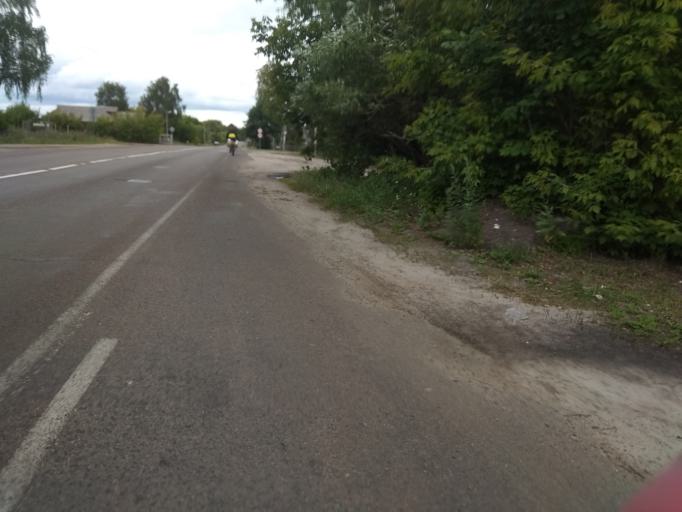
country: RU
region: Moskovskaya
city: Misheronskiy
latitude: 55.5988
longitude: 39.7048
